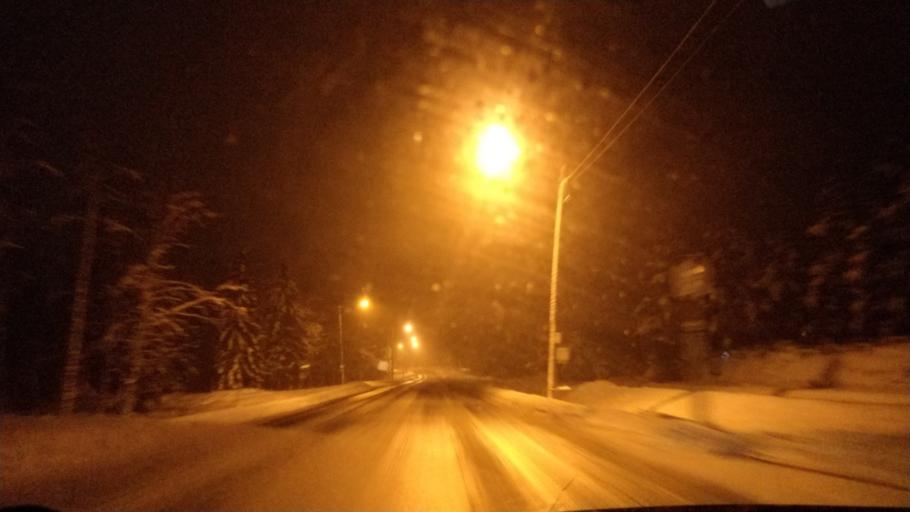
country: FI
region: Lapland
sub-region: Rovaniemi
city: Rovaniemi
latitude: 66.2772
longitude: 25.3323
